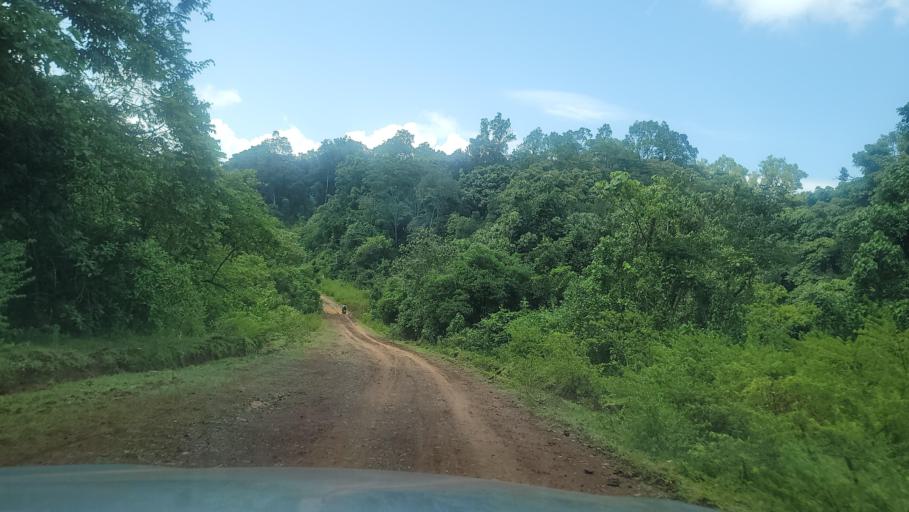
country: ET
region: Southern Nations, Nationalities, and People's Region
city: Bonga
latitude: 7.6712
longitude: 36.2432
